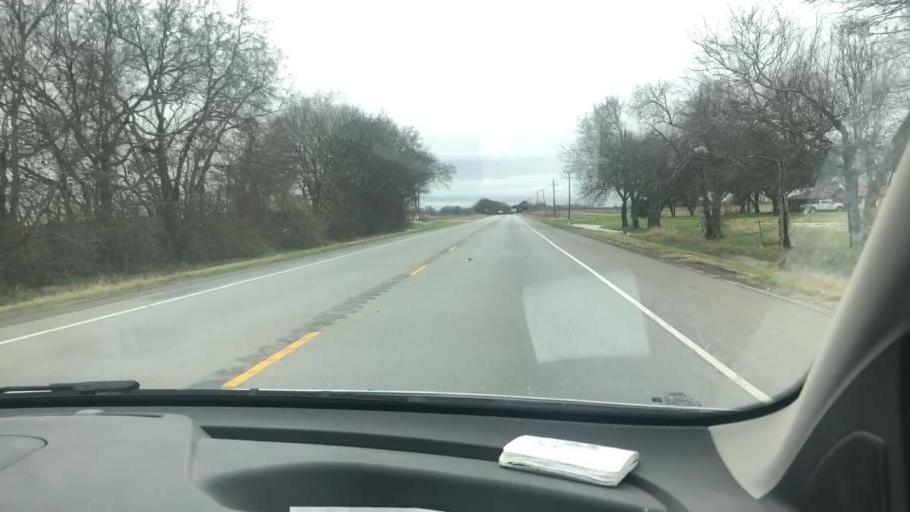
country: US
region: Texas
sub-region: Matagorda County
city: Bay City
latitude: 29.0696
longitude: -95.9714
